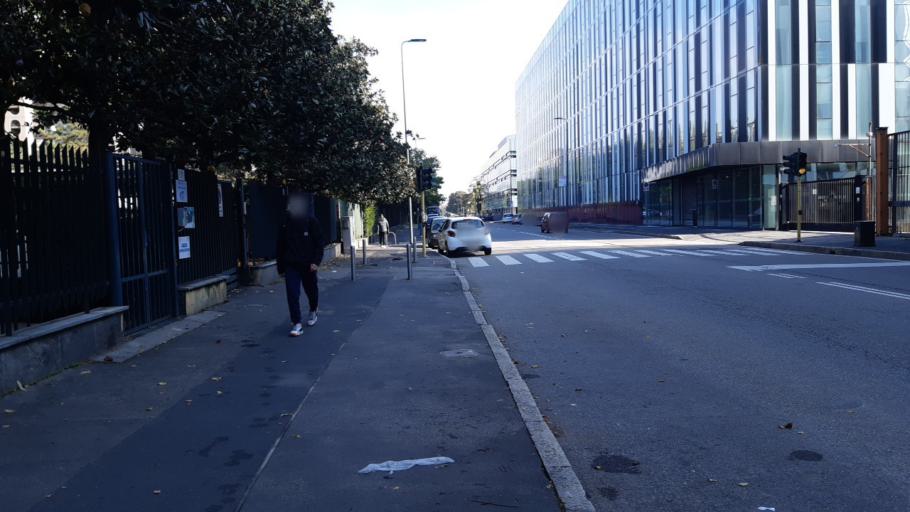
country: IT
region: Lombardy
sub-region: Citta metropolitana di Milano
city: Sesto San Giovanni
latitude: 45.5047
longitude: 9.2503
